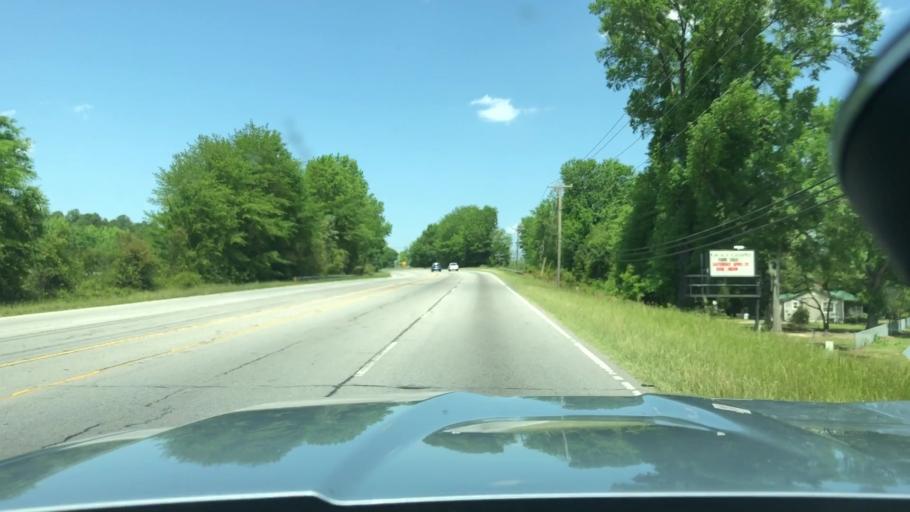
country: US
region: South Carolina
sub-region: Lexington County
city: Pineridge
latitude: 33.9065
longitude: -81.0658
